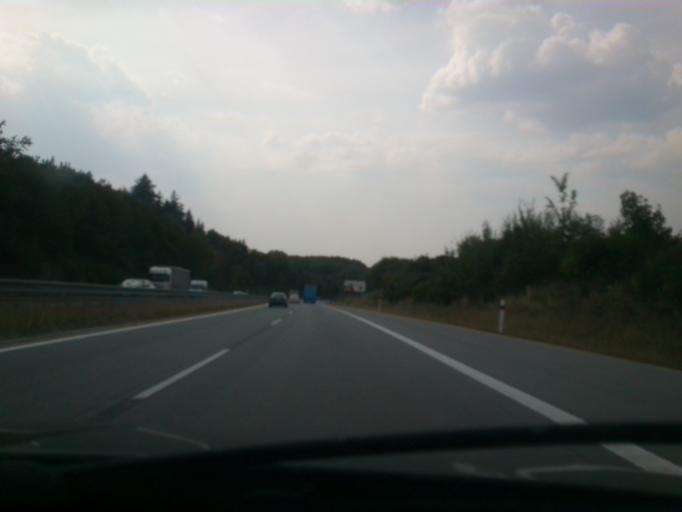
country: CZ
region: Central Bohemia
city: Trhovy Stepanov
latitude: 49.7585
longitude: 14.9634
